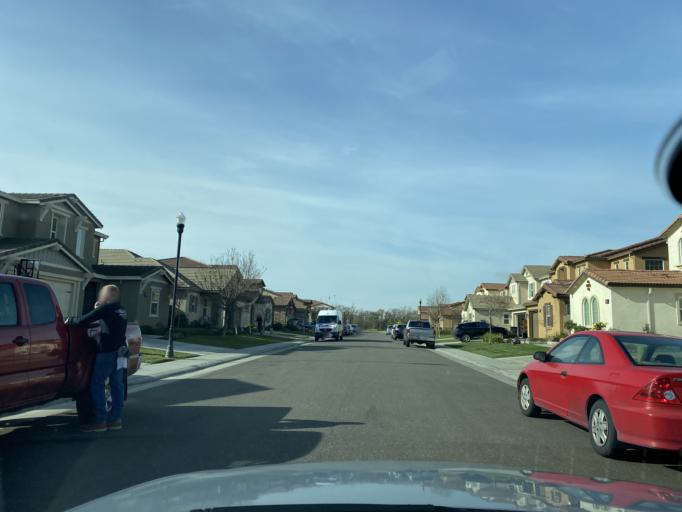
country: US
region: California
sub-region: Sacramento County
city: Elk Grove
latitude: 38.4028
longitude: -121.3972
